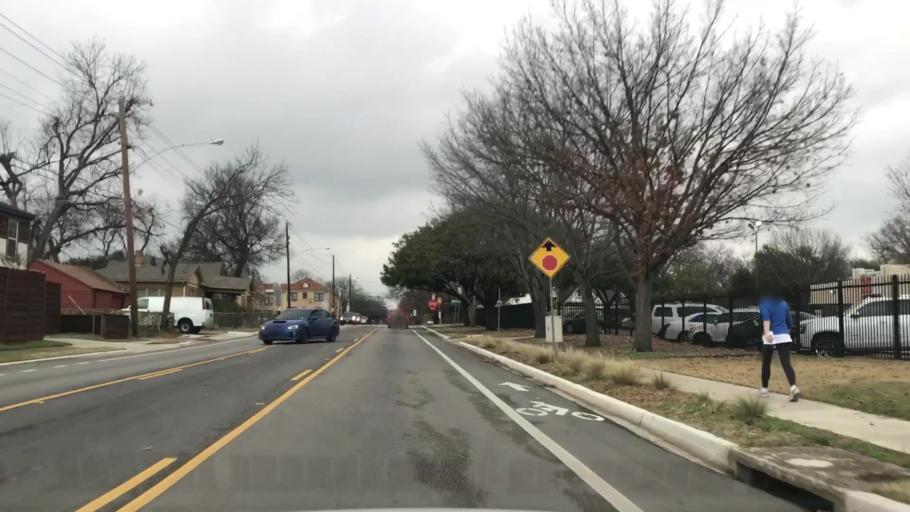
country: US
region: Texas
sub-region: Dallas County
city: Highland Park
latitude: 32.8240
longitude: -96.7680
